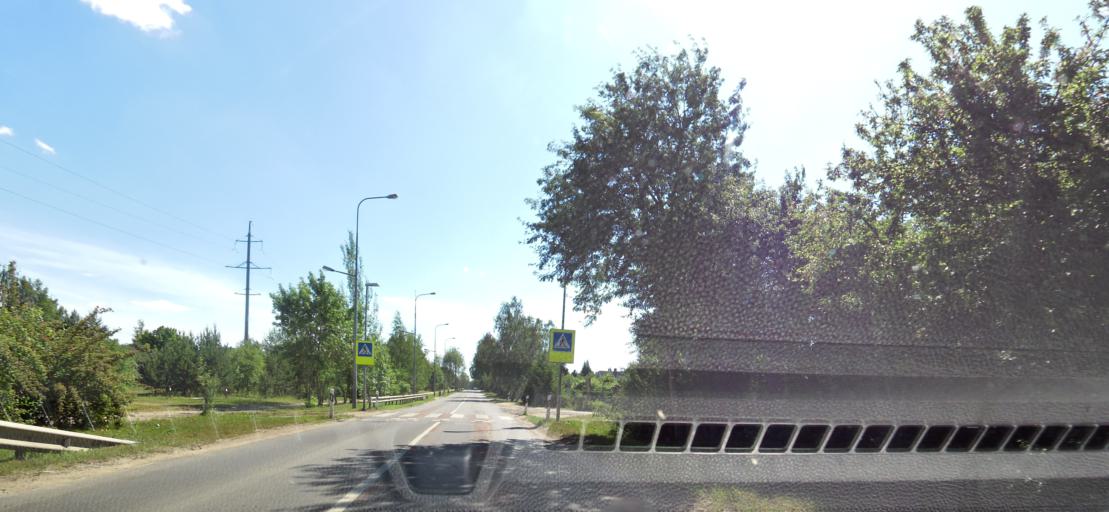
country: LT
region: Vilnius County
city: Rasos
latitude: 54.7854
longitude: 25.3468
